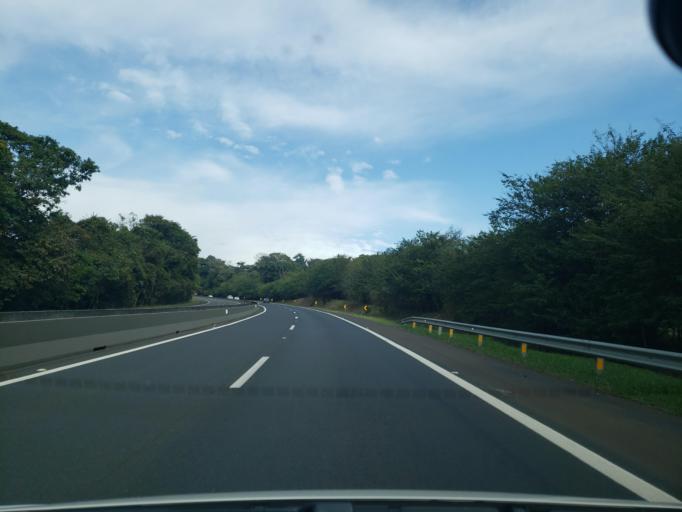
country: BR
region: Sao Paulo
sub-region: Brotas
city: Brotas
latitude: -22.2774
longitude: -47.9842
